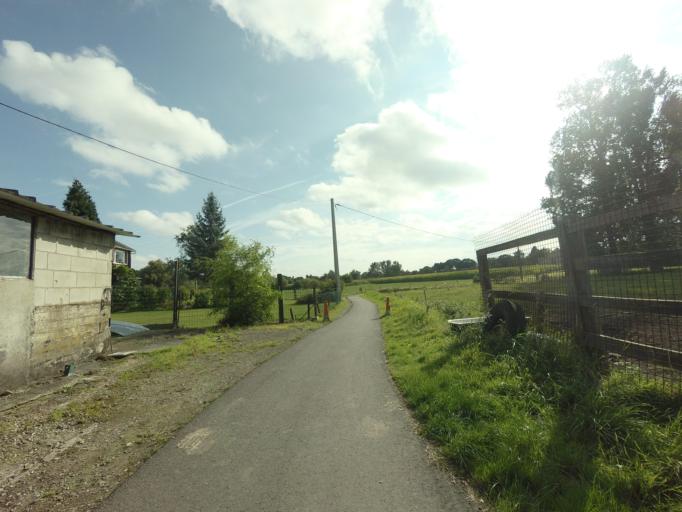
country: BE
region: Flanders
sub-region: Provincie Antwerpen
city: Aartselaar
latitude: 51.1129
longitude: 4.3962
